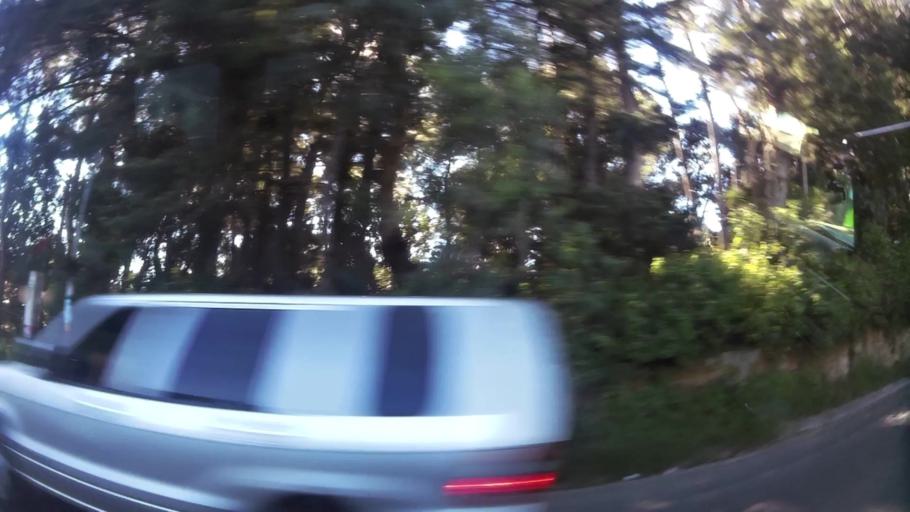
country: GT
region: Sacatepequez
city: Santa Lucia Milpas Altas
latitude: 14.5701
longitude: -90.6399
